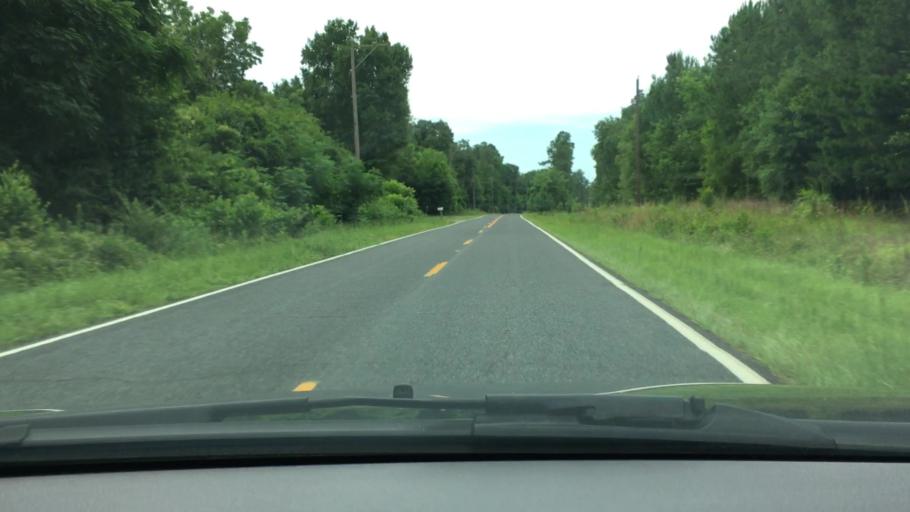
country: US
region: South Carolina
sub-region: Barnwell County
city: Williston
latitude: 33.6337
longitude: -81.3649
